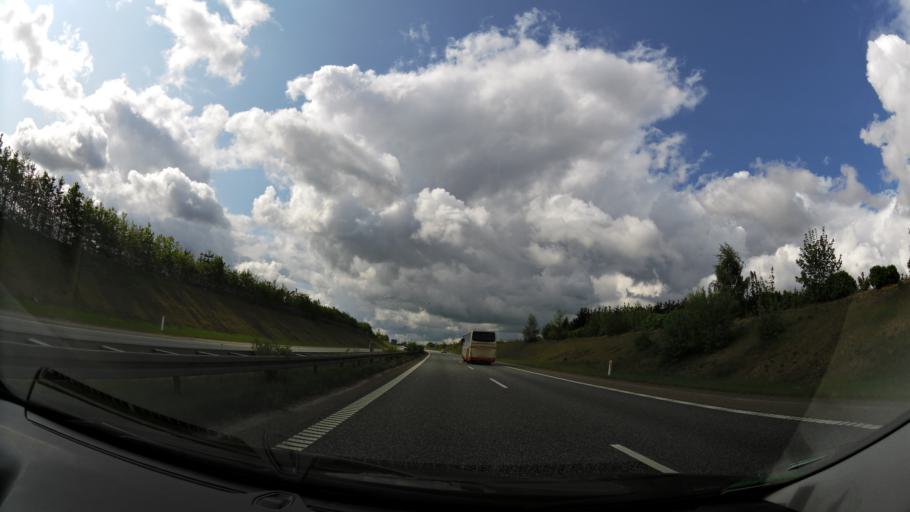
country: DK
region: South Denmark
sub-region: Odense Kommune
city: Hojby
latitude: 55.3178
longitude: 10.4405
